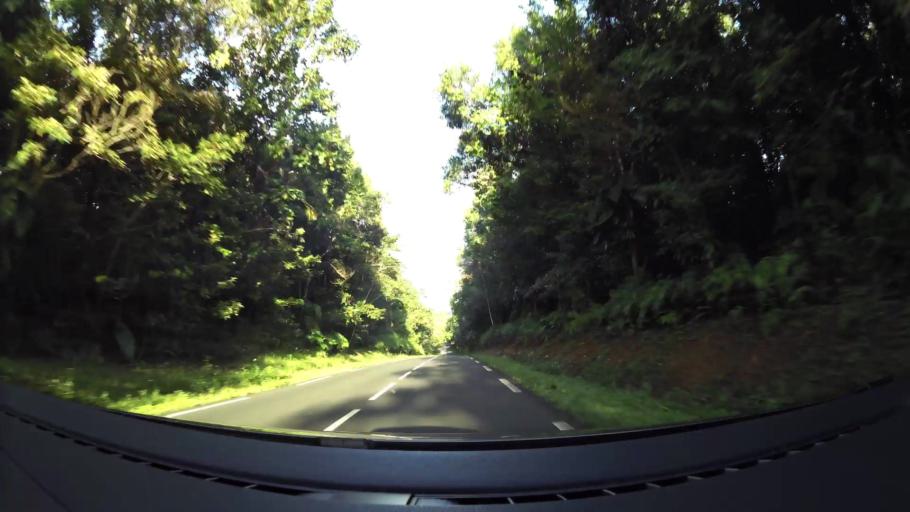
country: GP
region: Guadeloupe
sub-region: Guadeloupe
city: Petit-Bourg
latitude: 16.1808
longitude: -61.6852
